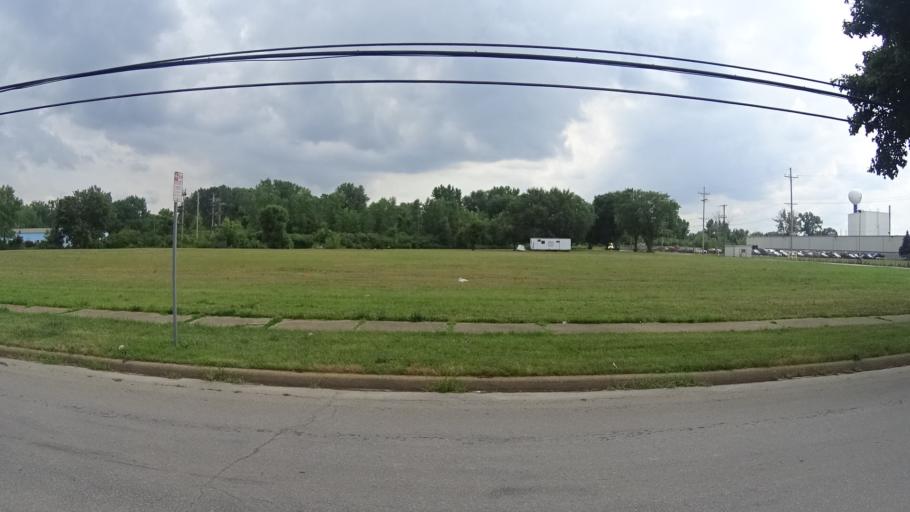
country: US
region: Ohio
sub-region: Erie County
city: Sandusky
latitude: 41.4461
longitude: -82.7401
